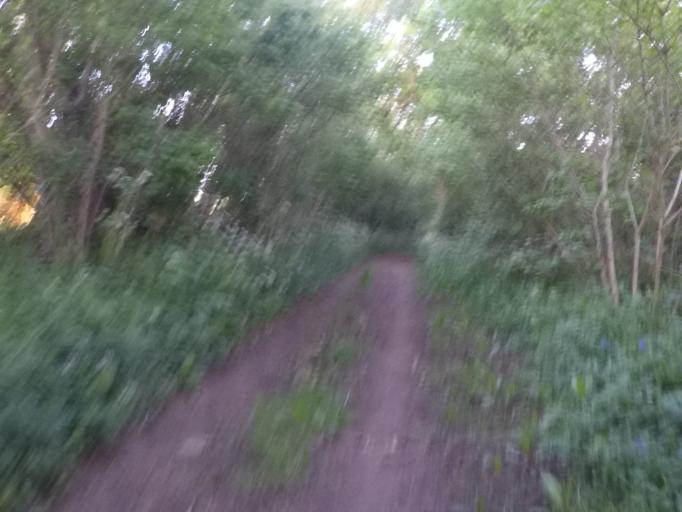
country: GB
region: England
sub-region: Oxfordshire
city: Charlbury
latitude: 51.8303
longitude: -1.5110
